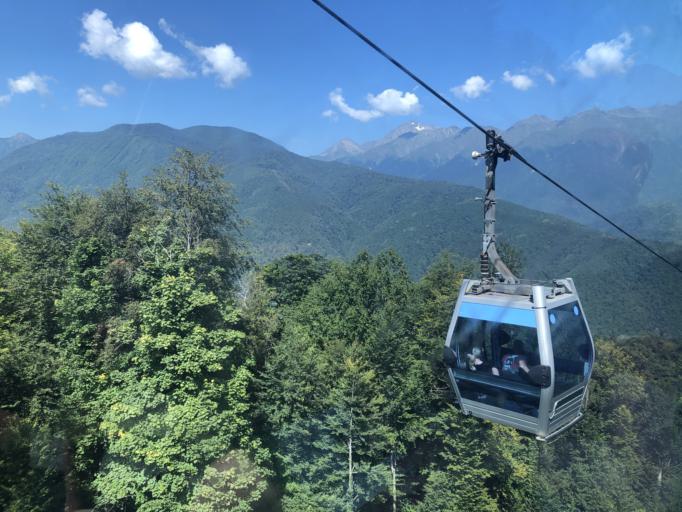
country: RU
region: Krasnodarskiy
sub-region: Sochi City
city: Krasnaya Polyana
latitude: 43.6708
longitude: 40.2602
